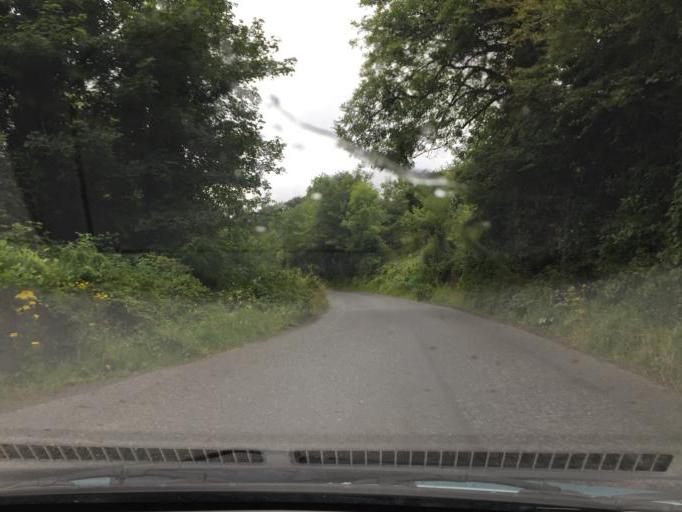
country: IE
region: Connaught
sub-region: Sligo
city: Sligo
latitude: 54.2366
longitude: -8.4513
